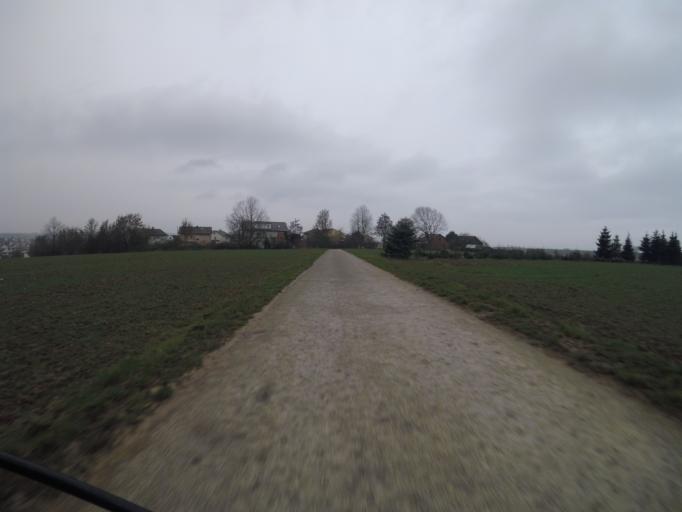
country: DE
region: Baden-Wuerttemberg
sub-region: Regierungsbezirk Stuttgart
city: Kirchberg an der Murr
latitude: 48.9466
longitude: 9.3489
